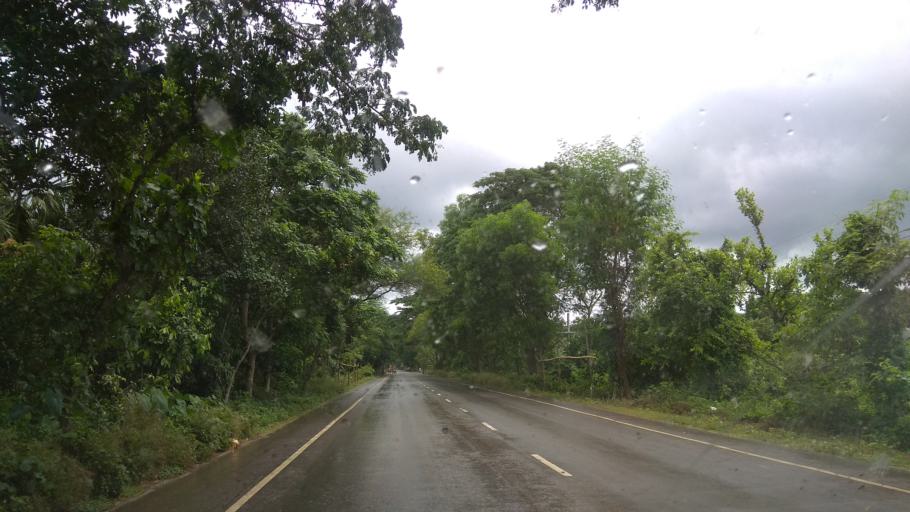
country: BD
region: Khulna
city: Kalia
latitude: 23.2478
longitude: 89.7567
